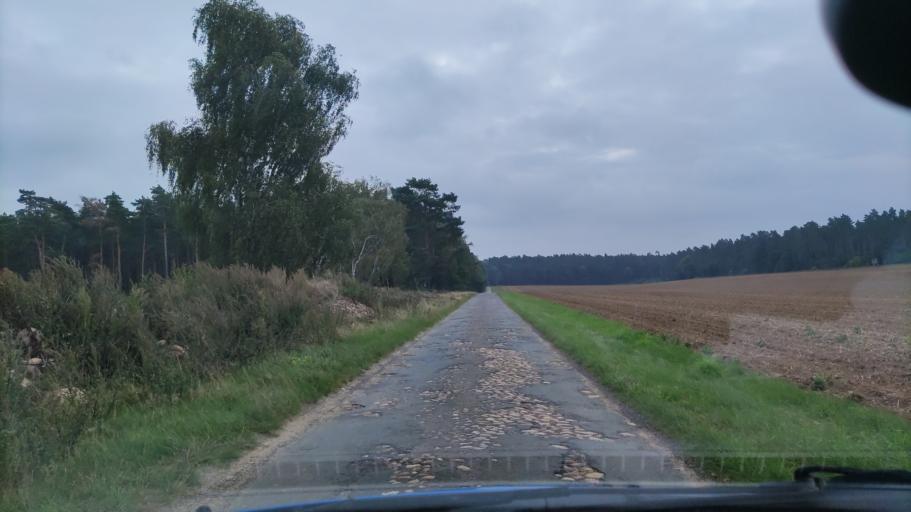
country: DE
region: Lower Saxony
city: Altenmedingen
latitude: 53.1572
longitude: 10.5723
